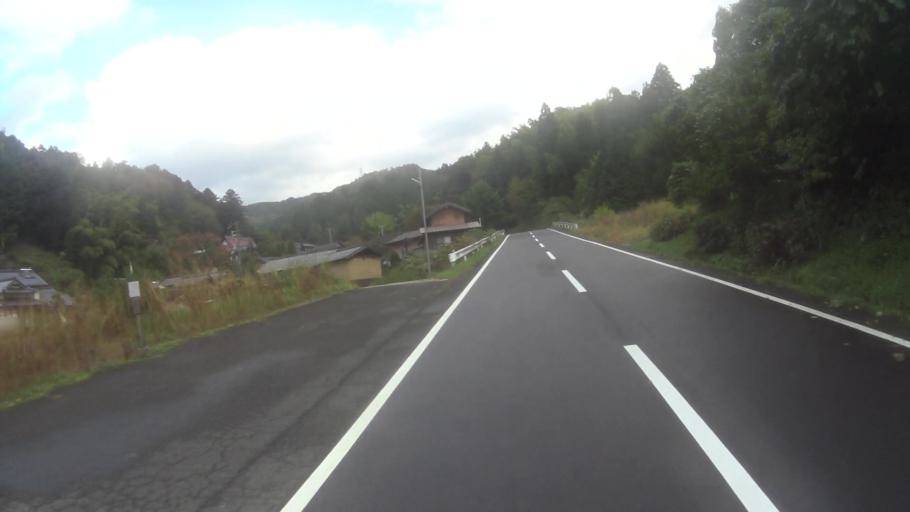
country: JP
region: Kyoto
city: Miyazu
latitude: 35.5019
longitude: 135.1348
